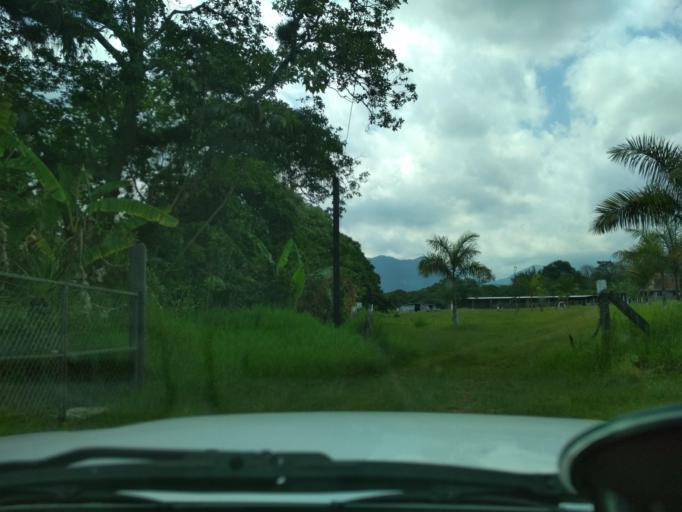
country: MX
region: Veracruz
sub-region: Fortin
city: Monte Salas
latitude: 18.9277
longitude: -97.0132
